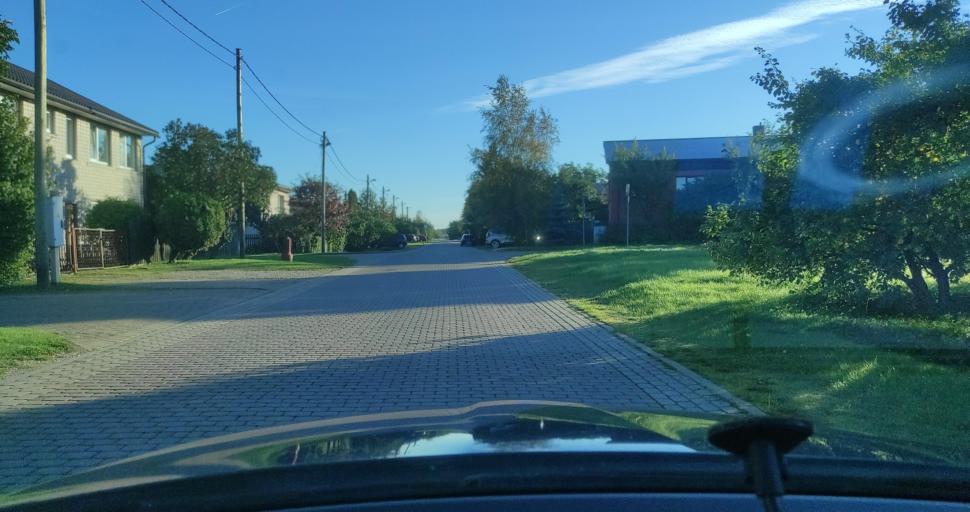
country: LV
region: Ventspils
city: Ventspils
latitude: 57.3722
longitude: 21.5766
